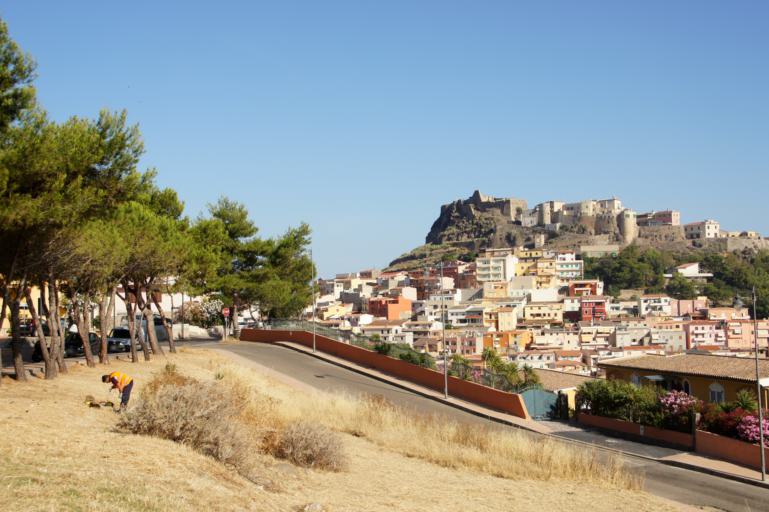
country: IT
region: Sardinia
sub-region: Provincia di Sassari
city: Castelsardo
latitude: 40.9117
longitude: 8.7183
